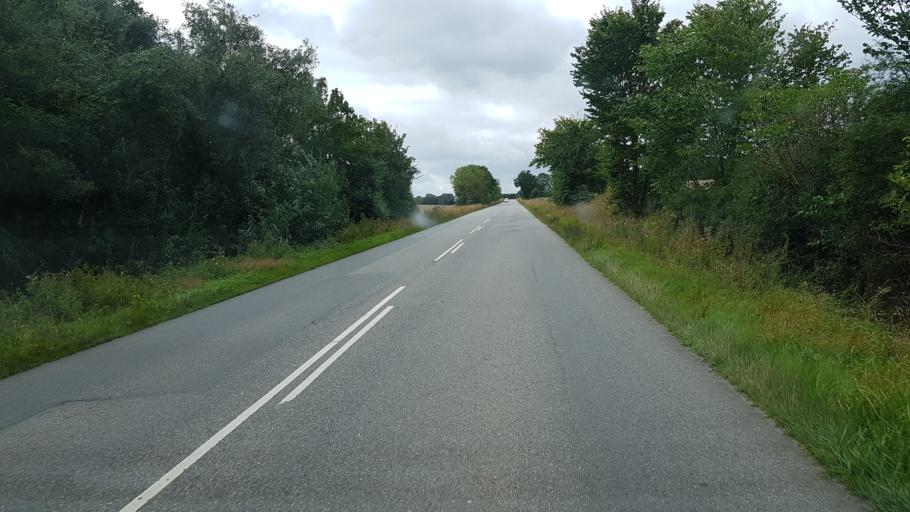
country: DK
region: South Denmark
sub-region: Kolding Kommune
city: Kolding
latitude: 55.4774
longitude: 9.4070
